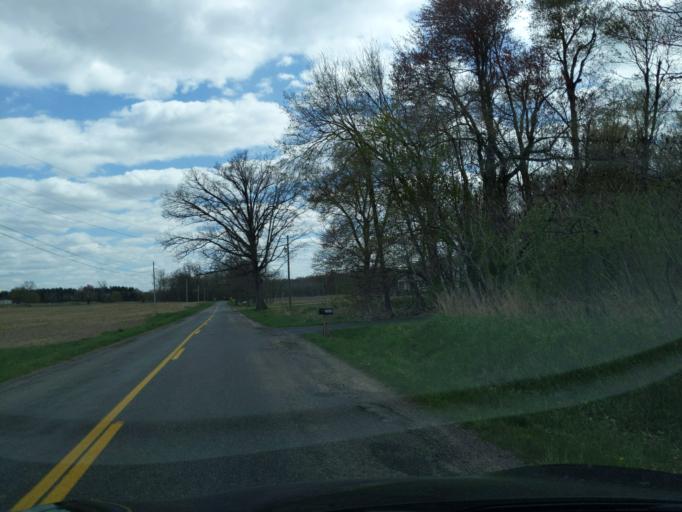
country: US
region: Michigan
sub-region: Eaton County
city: Eaton Rapids
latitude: 42.5134
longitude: -84.5420
